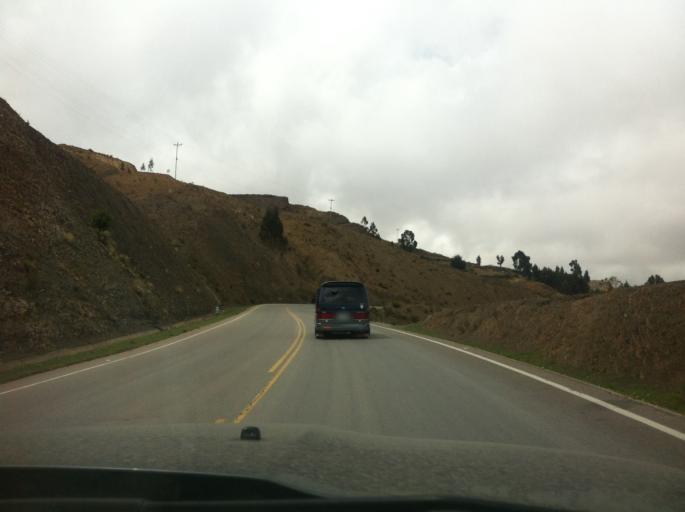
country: BO
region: Cochabamba
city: Sipe Sipe
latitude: -17.6492
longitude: -66.4783
